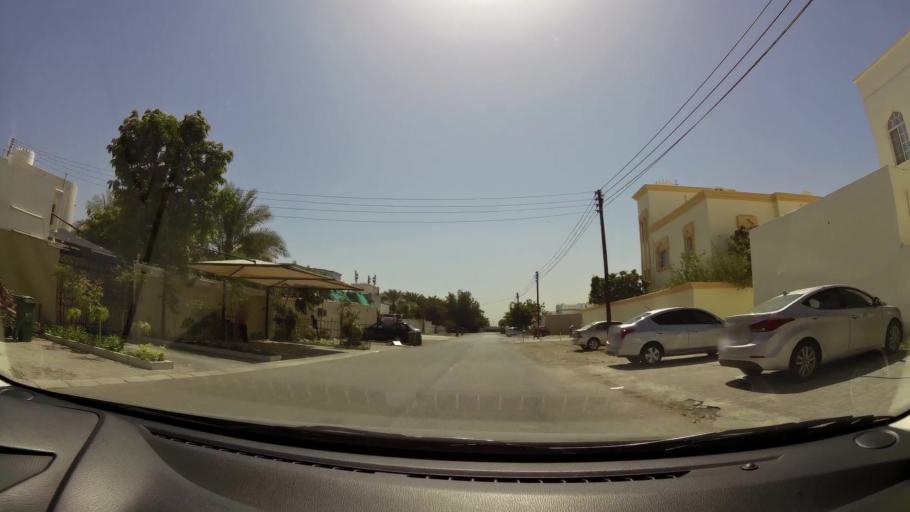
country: OM
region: Muhafazat Masqat
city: As Sib al Jadidah
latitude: 23.6030
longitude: 58.2453
